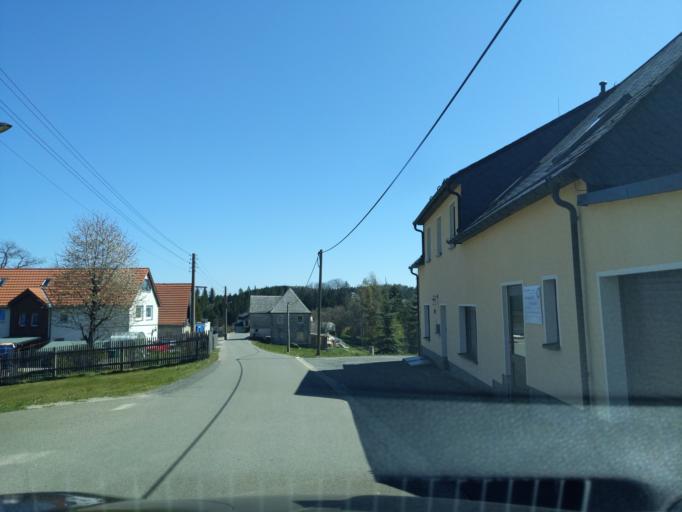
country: DE
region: Saxony
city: Stutzengrun
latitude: 50.5303
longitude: 12.5414
